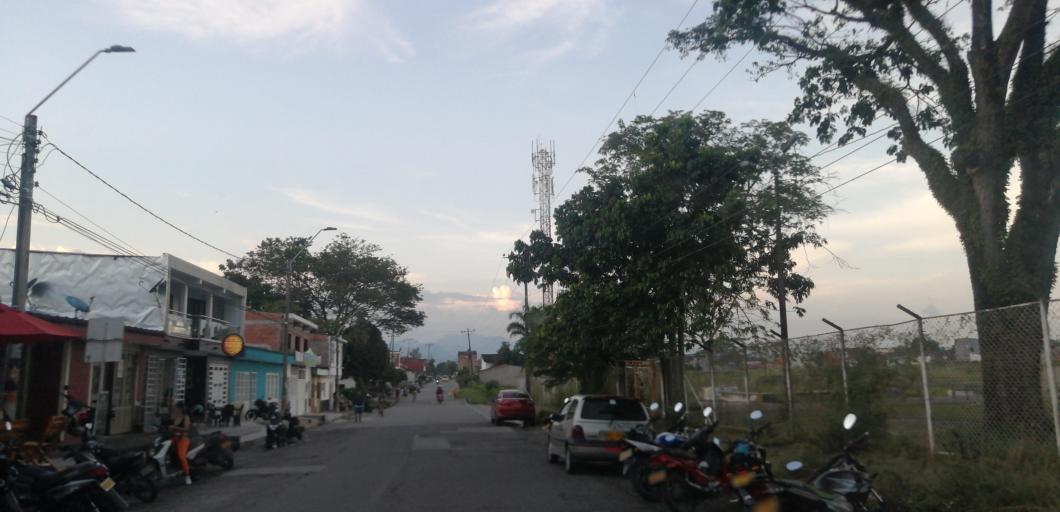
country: CO
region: Meta
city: Acacias
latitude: 3.9917
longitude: -73.7570
